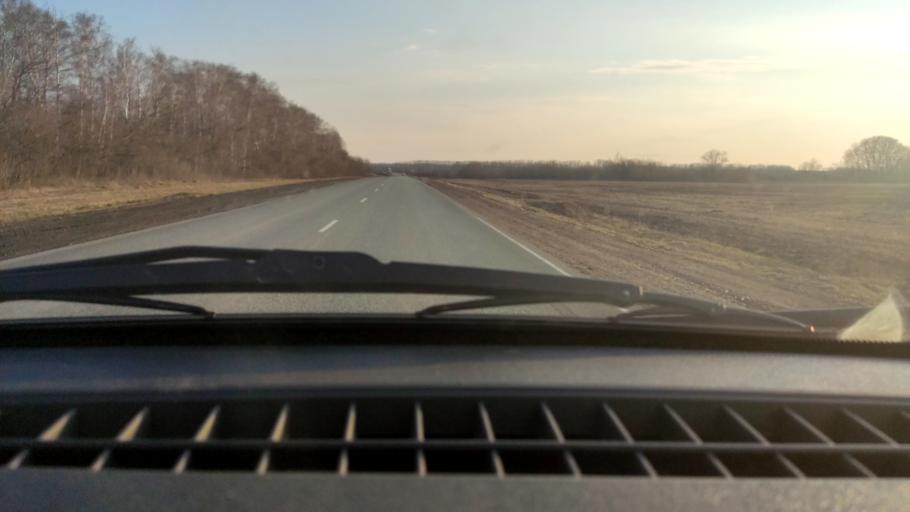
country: RU
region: Bashkortostan
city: Chishmy
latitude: 54.5311
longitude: 55.3072
